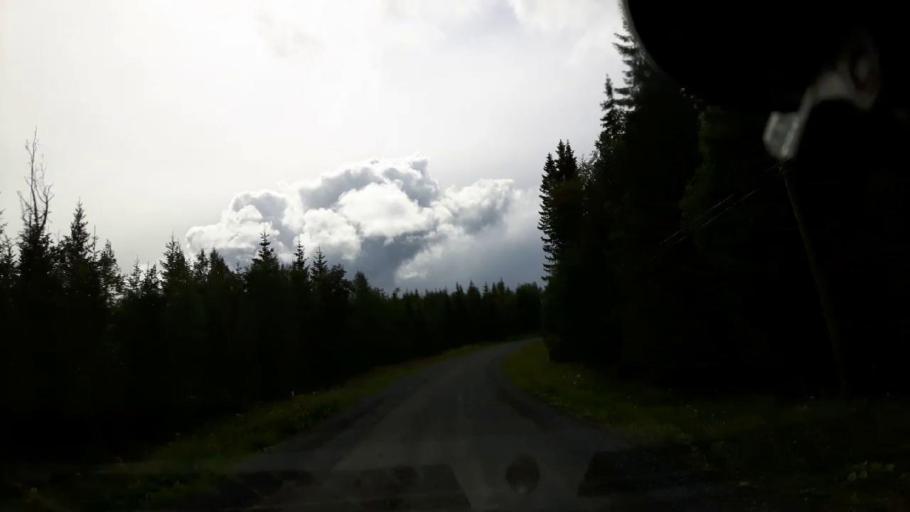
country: SE
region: Jaemtland
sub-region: Krokoms Kommun
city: Valla
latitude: 63.3573
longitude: 13.8534
